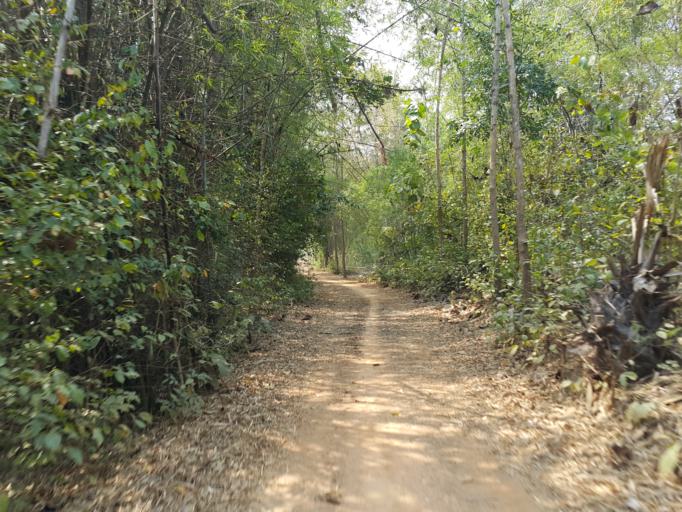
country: TH
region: Sukhothai
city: Thung Saliam
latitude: 17.3151
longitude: 99.5019
